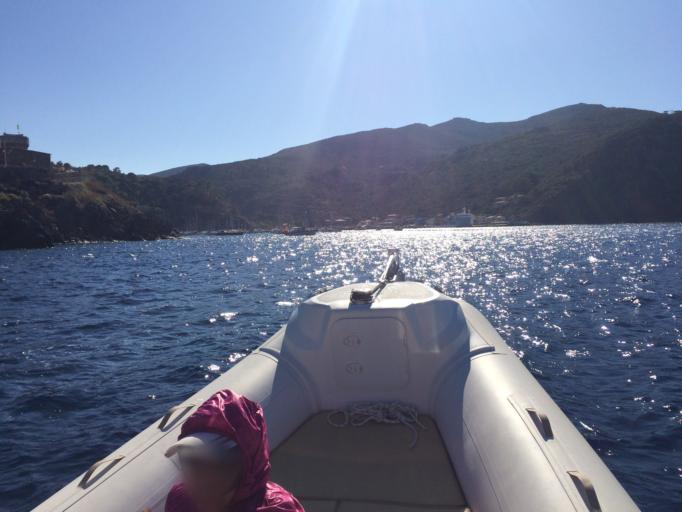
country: IT
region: Tuscany
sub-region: Provincia di Livorno
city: Capraia Isola
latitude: 43.0523
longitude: 9.8445
